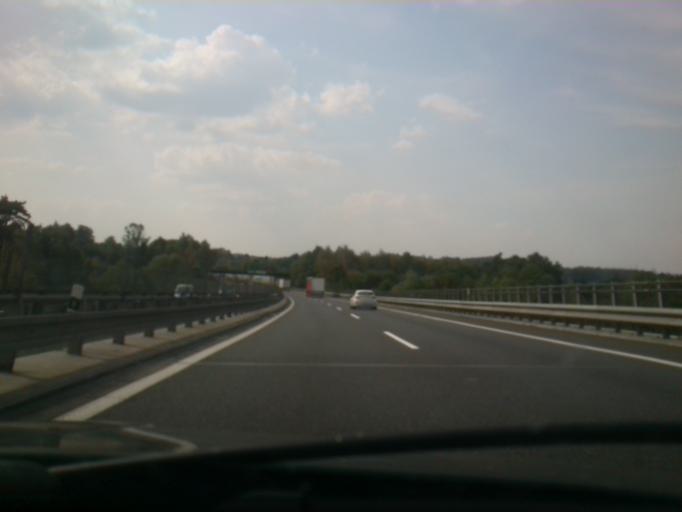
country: CZ
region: Central Bohemia
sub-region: Okres Praha-Vychod
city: Mnichovice
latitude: 49.9091
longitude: 14.7289
